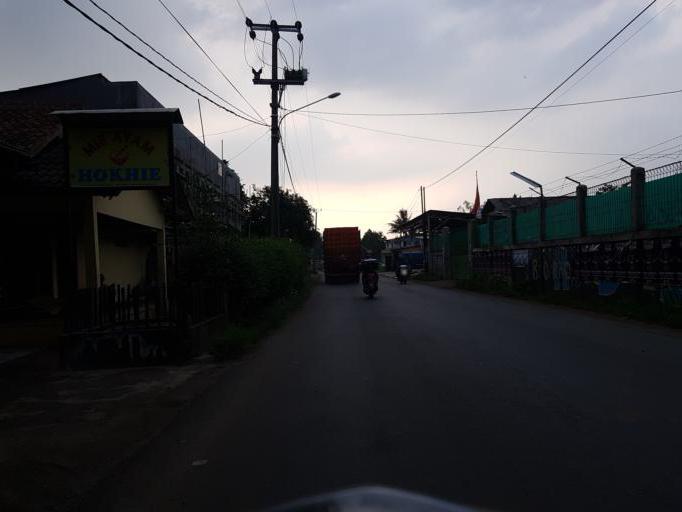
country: ID
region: West Java
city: Parung
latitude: -6.4754
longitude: 106.7269
